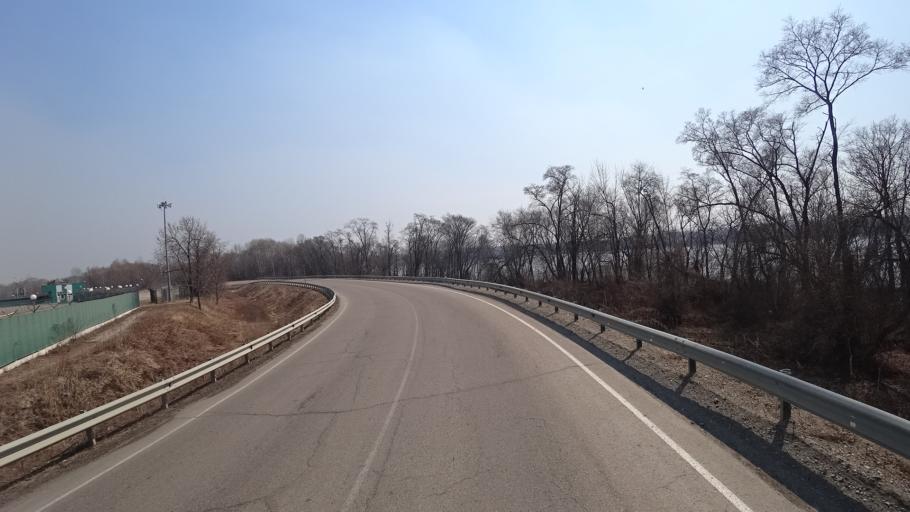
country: RU
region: Amur
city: Novobureyskiy
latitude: 49.7833
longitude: 129.9226
